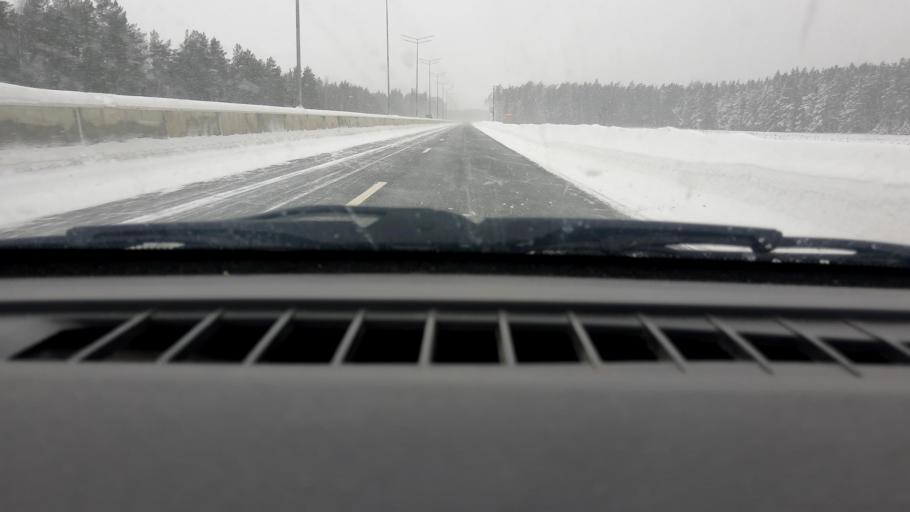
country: RU
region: Moskovskaya
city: Krasnoarmeysk
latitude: 56.0236
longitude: 38.2344
